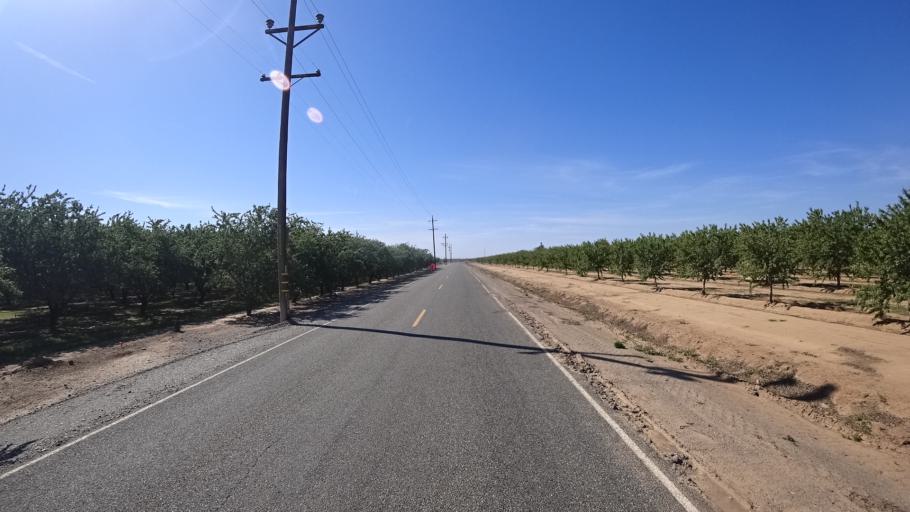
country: US
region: California
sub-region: Glenn County
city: Willows
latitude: 39.6273
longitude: -122.1783
